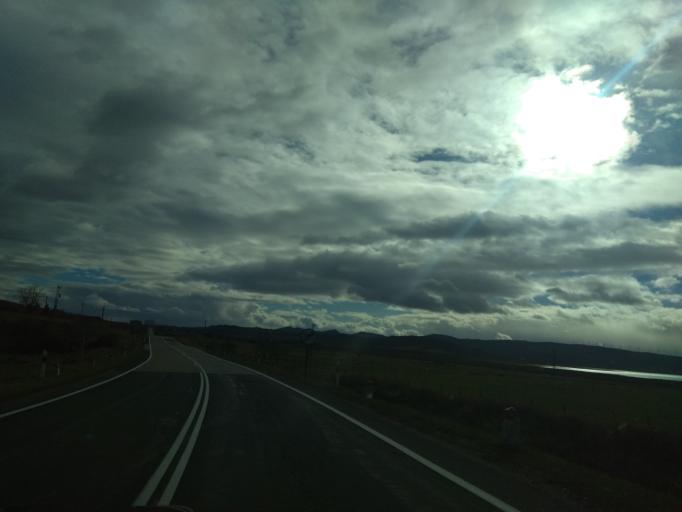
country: ES
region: Castille and Leon
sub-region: Provincia de Burgos
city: Arija
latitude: 43.0281
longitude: -3.8630
